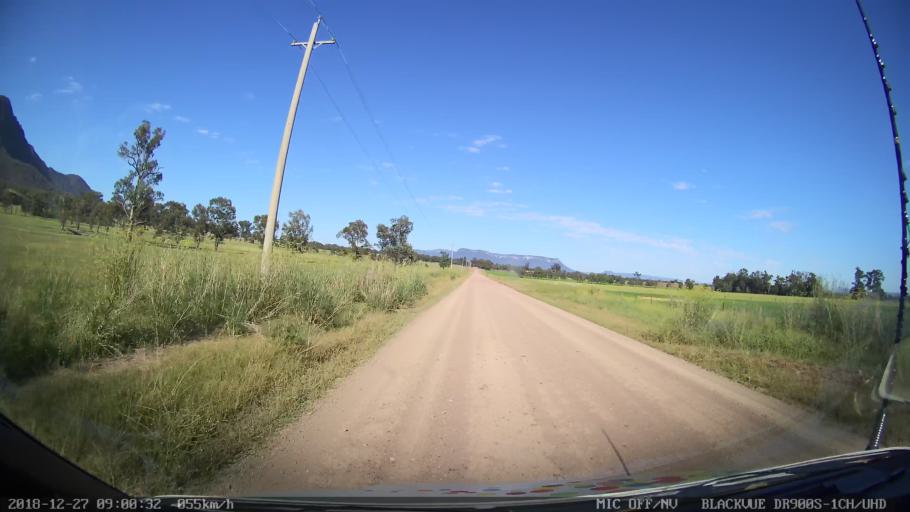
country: AU
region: New South Wales
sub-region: Lithgow
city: Portland
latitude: -33.1011
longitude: 150.2257
